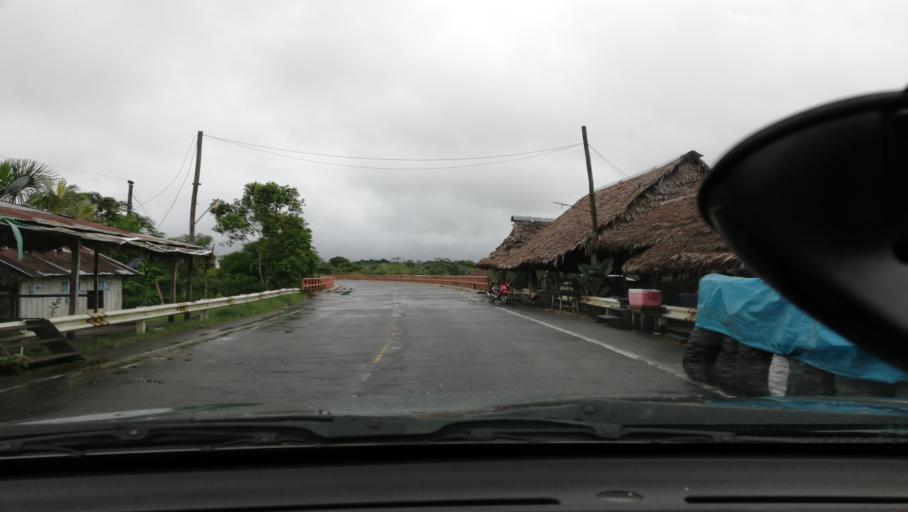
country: PE
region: Loreto
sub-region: Provincia de Loreto
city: Nauta
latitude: -4.2272
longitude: -73.4827
